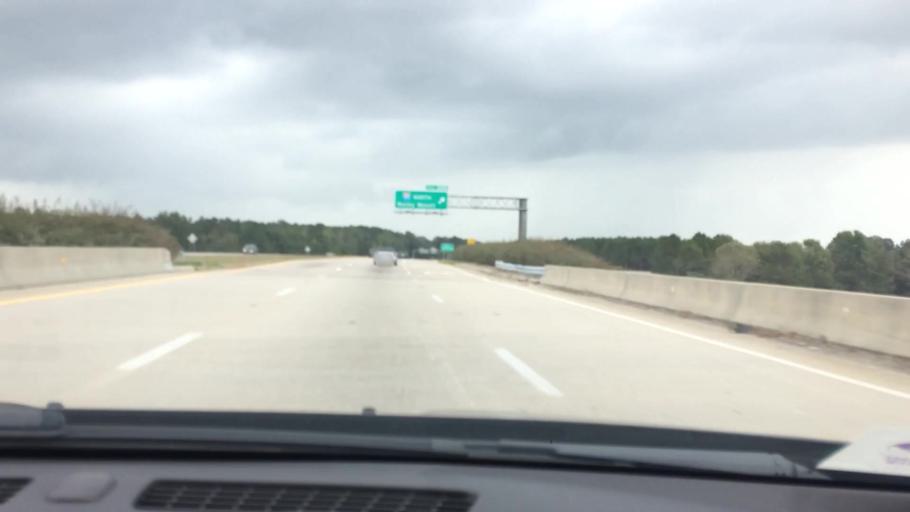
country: US
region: North Carolina
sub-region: Wilson County
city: Lucama
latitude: 35.7339
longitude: -78.0116
